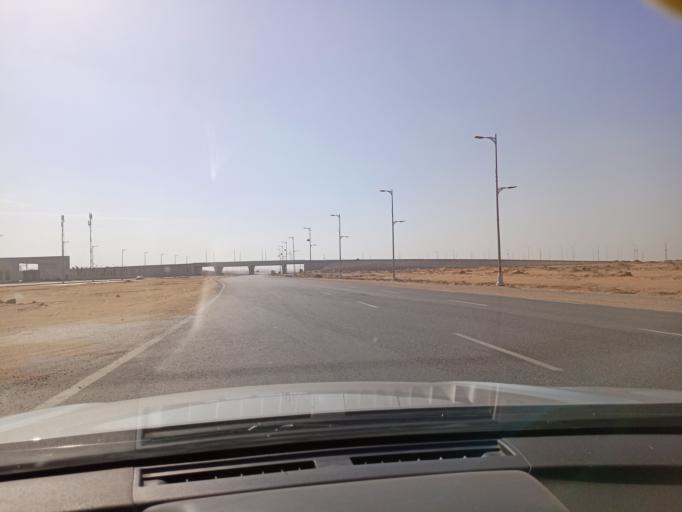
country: EG
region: Muhafazat al Qalyubiyah
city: Al Khankah
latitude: 30.0444
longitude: 31.6905
